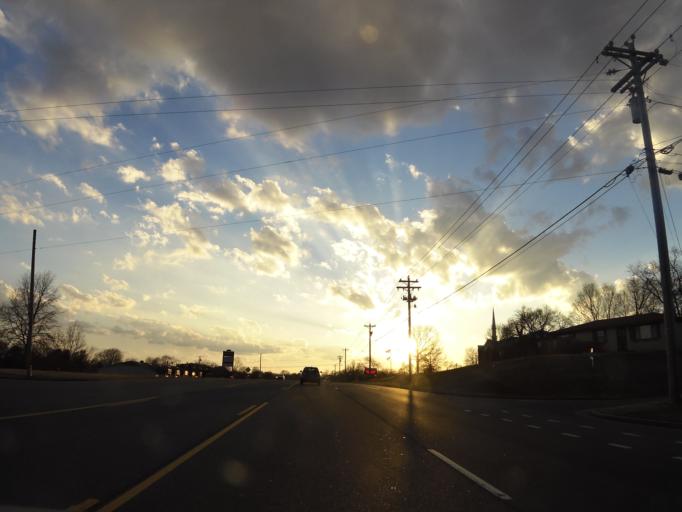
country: US
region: Tennessee
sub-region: Wilson County
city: Green Hill
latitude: 36.2237
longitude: -86.5455
